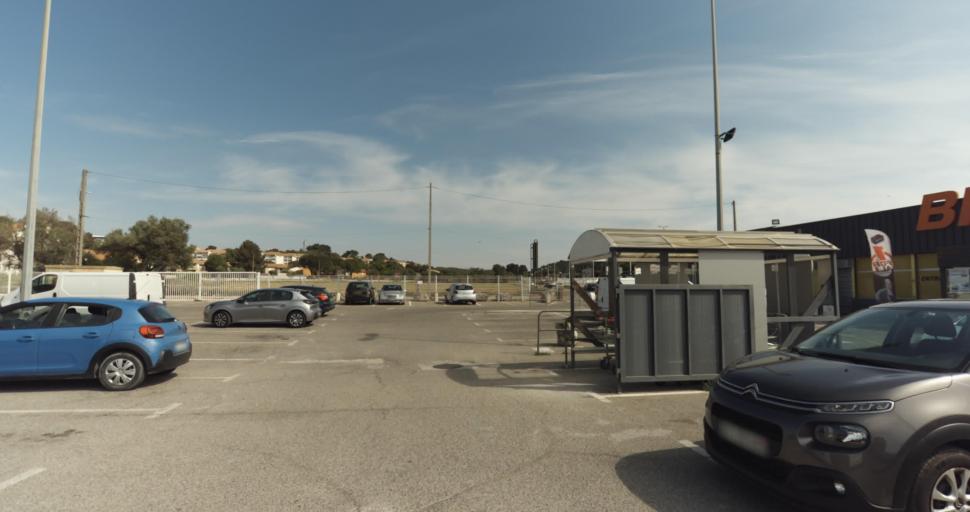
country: FR
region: Languedoc-Roussillon
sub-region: Departement du Gard
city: Rodilhan
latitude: 43.8561
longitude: 4.4022
